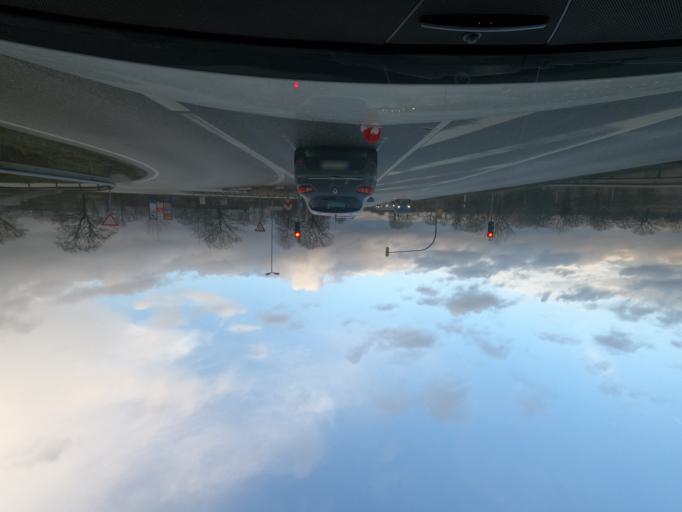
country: DE
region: Schleswig-Holstein
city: Alveslohe
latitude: 53.8055
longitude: 9.9392
